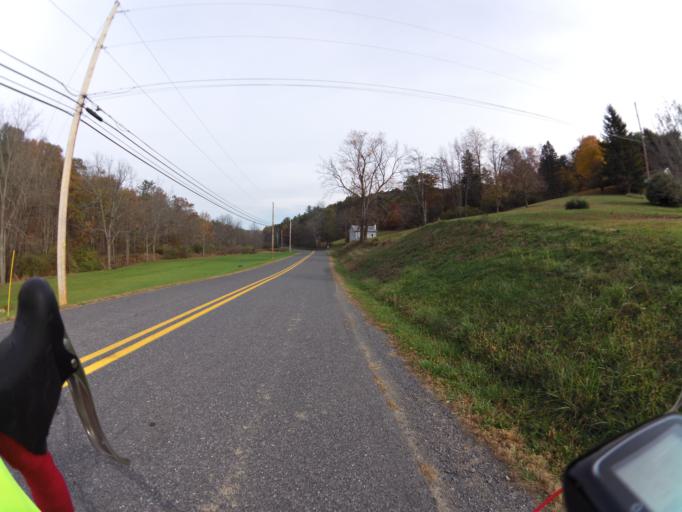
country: US
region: Pennsylvania
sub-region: Union County
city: New Columbia
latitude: 41.0323
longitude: -76.9212
